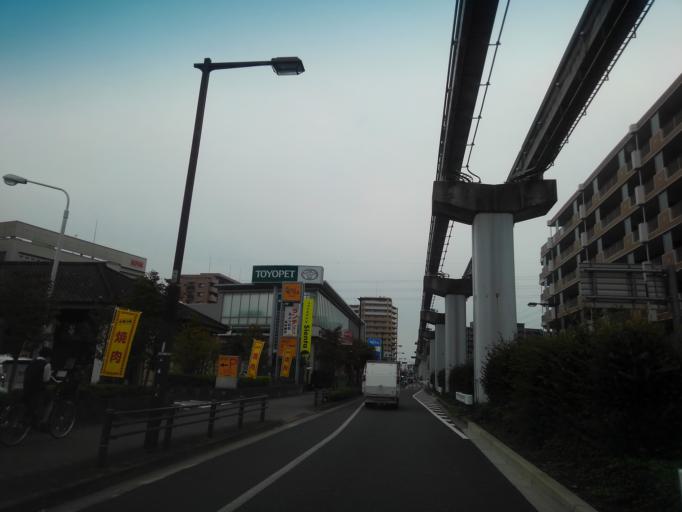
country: JP
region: Tokyo
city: Higashimurayama-shi
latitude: 35.7379
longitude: 139.4169
